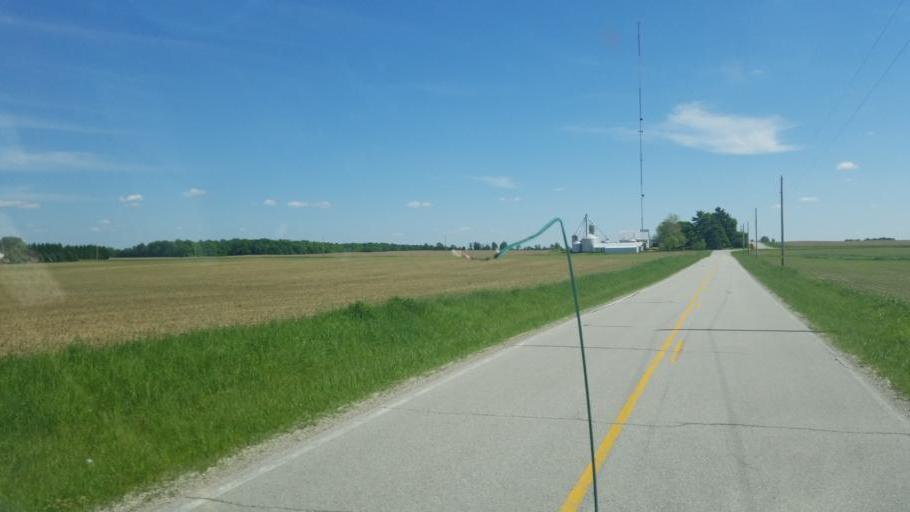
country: US
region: Ohio
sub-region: Crawford County
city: Bucyrus
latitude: 40.9090
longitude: -83.0549
